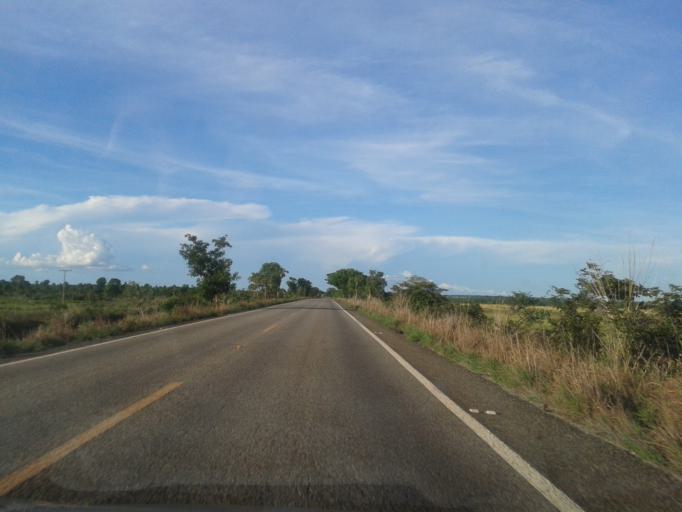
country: BR
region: Goias
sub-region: Sao Miguel Do Araguaia
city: Sao Miguel do Araguaia
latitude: -13.5780
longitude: -50.3147
